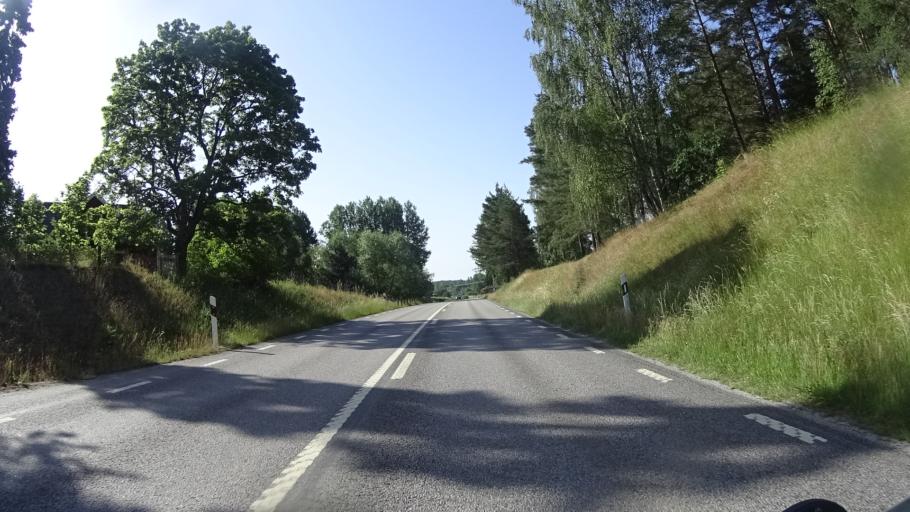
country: SE
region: OEstergoetland
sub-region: Linkopings Kommun
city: Sturefors
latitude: 58.3182
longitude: 15.8701
